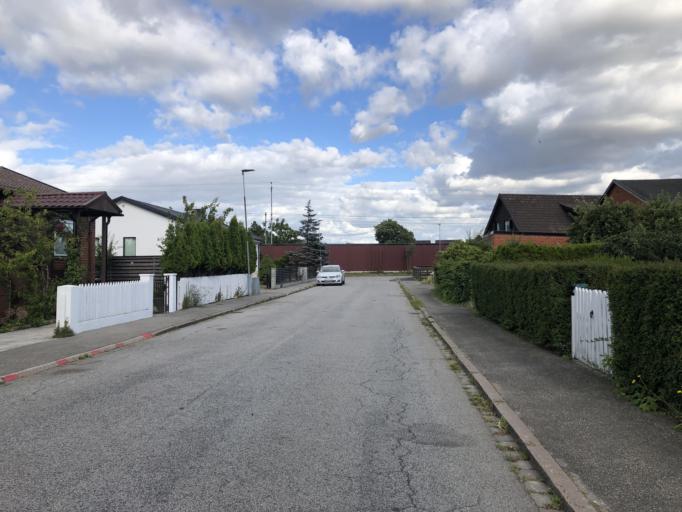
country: SE
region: Skane
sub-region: Malmo
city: Malmoe
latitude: 55.5728
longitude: 13.0288
